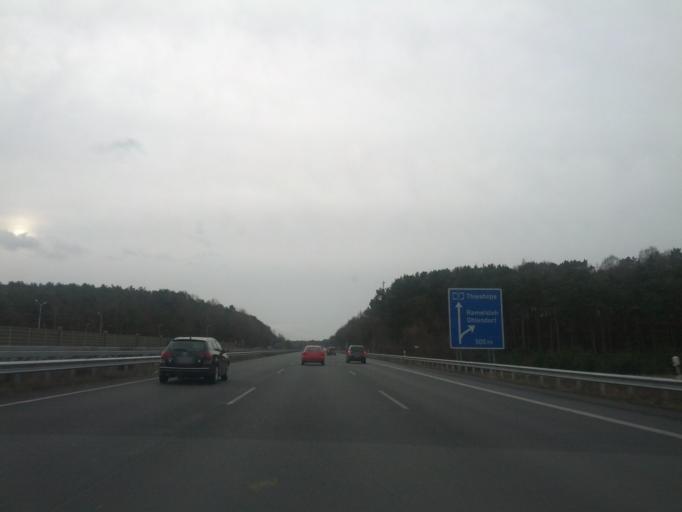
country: DE
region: Lower Saxony
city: Marxen
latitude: 53.3483
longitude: 10.0381
